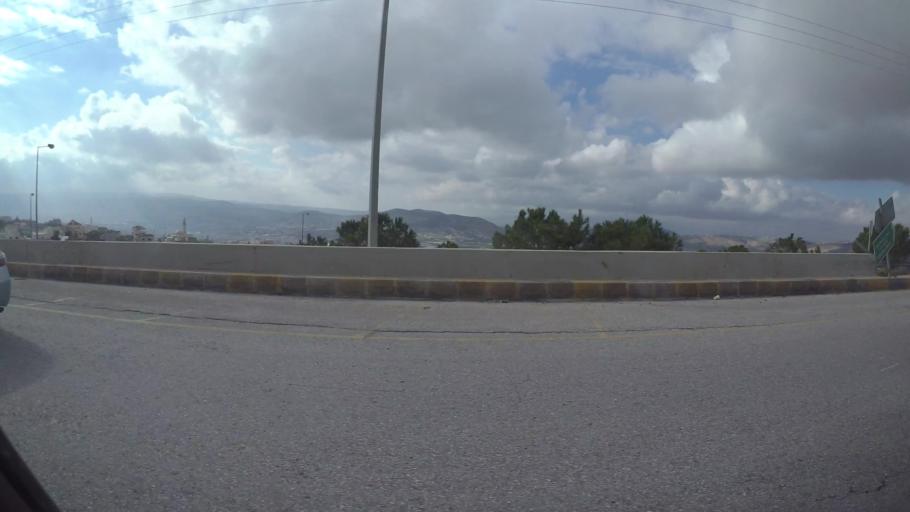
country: JO
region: Amman
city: Al Jubayhah
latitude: 32.0706
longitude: 35.8754
